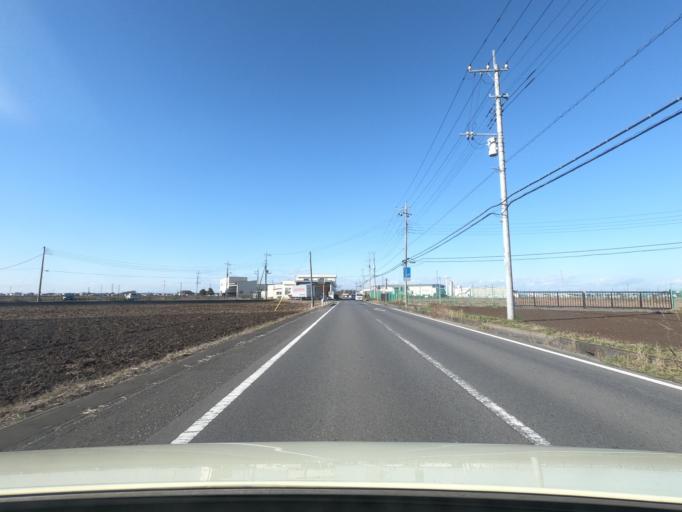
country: JP
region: Ibaraki
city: Ishige
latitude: 36.1636
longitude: 139.9920
